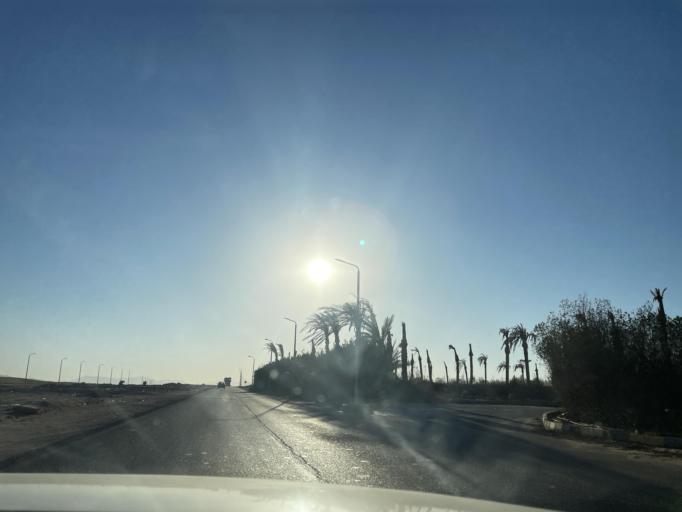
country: EG
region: Red Sea
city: Hurghada
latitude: 27.2178
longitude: 33.7954
